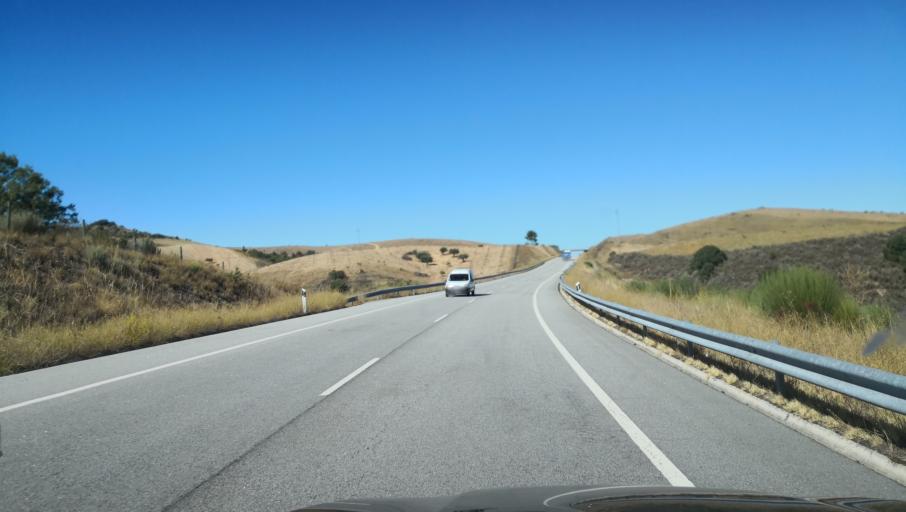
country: PT
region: Braganca
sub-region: Mirandela
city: Mirandela
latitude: 41.5222
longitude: -7.2412
